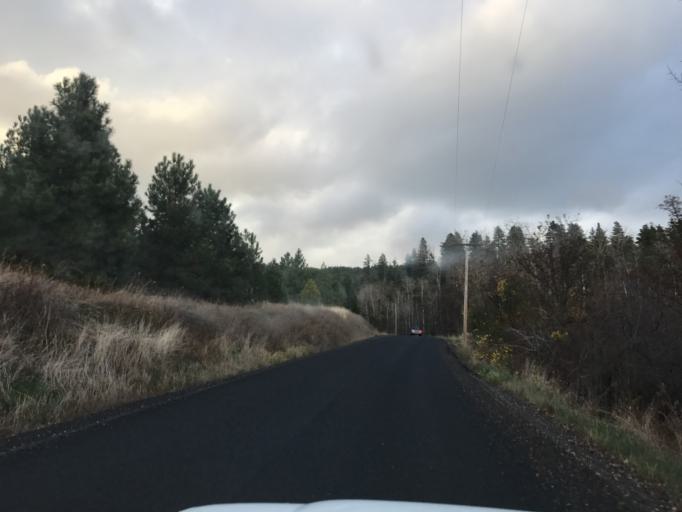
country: US
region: Idaho
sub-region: Latah County
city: Moscow
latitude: 46.7962
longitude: -116.9588
